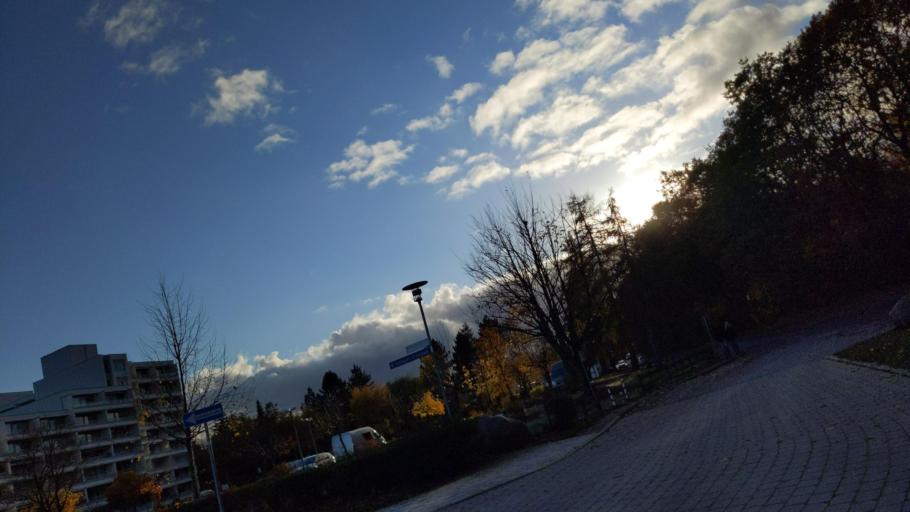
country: DE
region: Schleswig-Holstein
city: Sierksdorf
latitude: 54.0744
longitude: 10.7830
